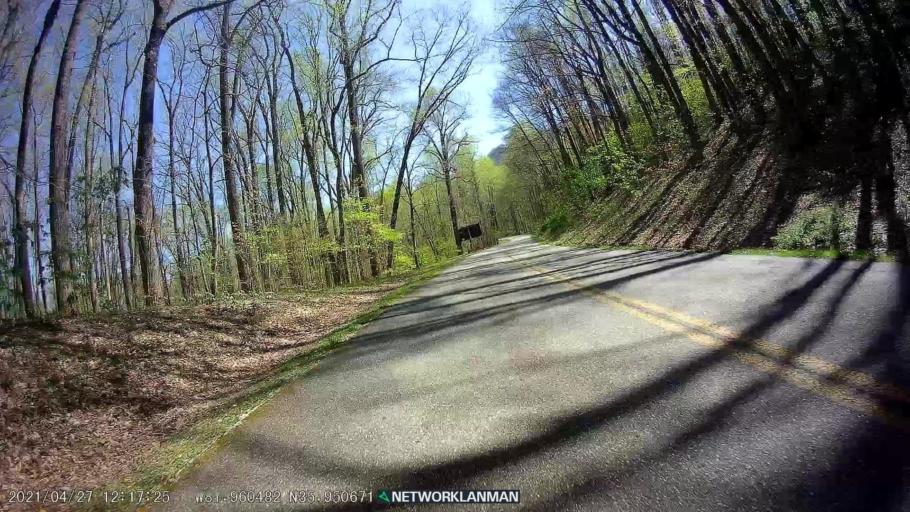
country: US
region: North Carolina
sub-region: Mitchell County
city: Spruce Pine
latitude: 35.9508
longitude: -81.9605
